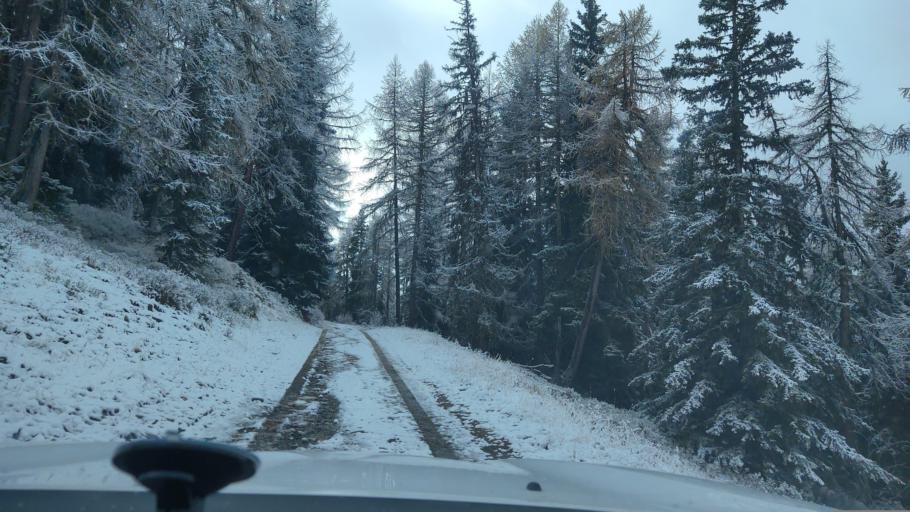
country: FR
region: Rhone-Alpes
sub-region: Departement de la Savoie
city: Seez
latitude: 45.5918
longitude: 6.8041
